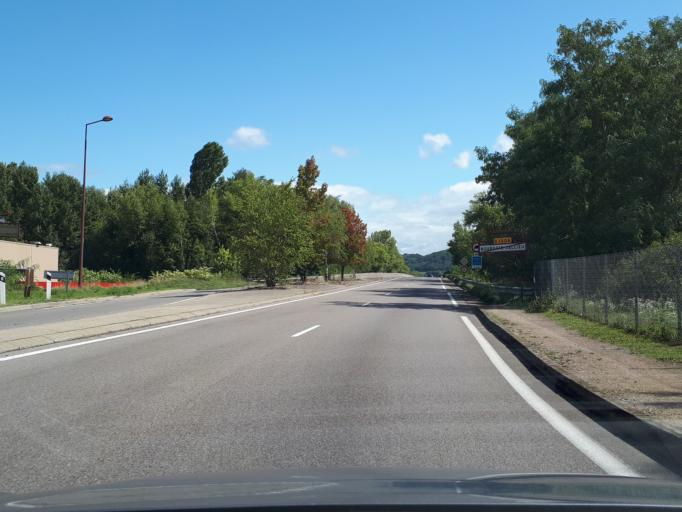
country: FR
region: Rhone-Alpes
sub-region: Departement de l'Isere
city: Bourgoin
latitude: 45.5840
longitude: 5.2999
